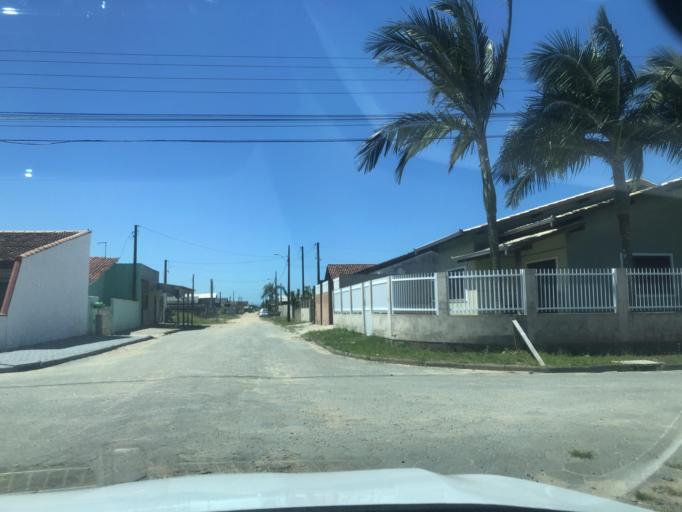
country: BR
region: Santa Catarina
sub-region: Sao Francisco Do Sul
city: Sao Francisco do Sul
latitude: -26.2331
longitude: -48.5206
